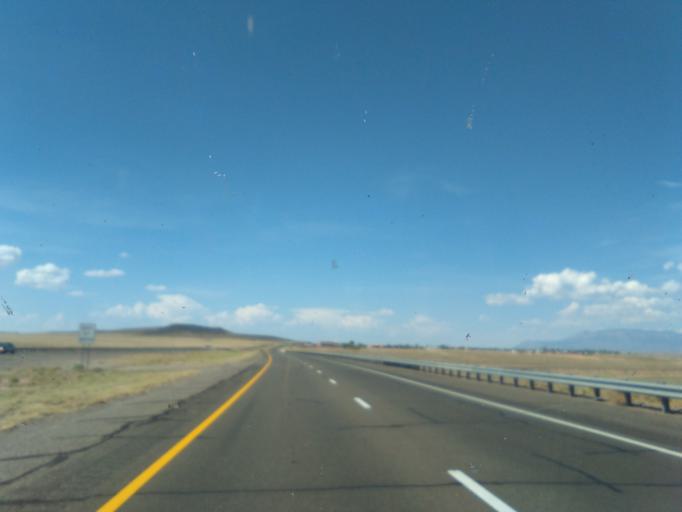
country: US
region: New Mexico
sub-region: Valencia County
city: Bosque Farms
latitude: 34.8861
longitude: -106.7277
